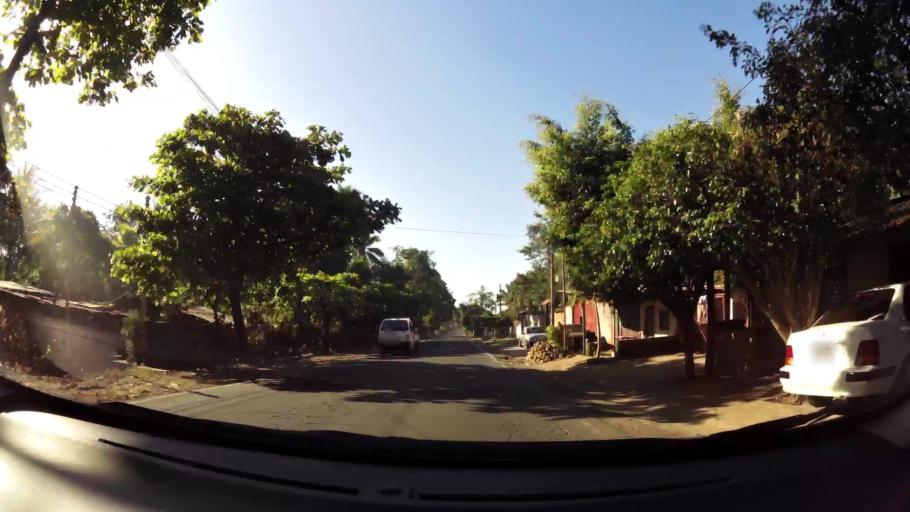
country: SV
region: Sonsonate
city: Sonzacate
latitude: 13.7450
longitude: -89.7084
